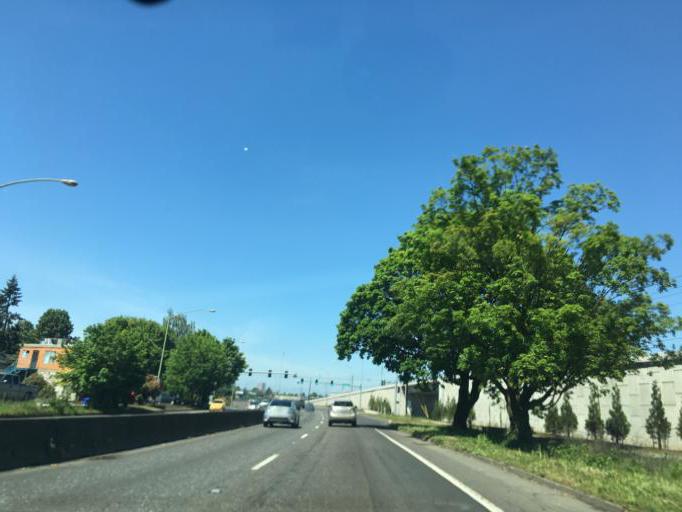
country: US
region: Oregon
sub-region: Clackamas County
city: Milwaukie
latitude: 45.4819
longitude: -122.6425
